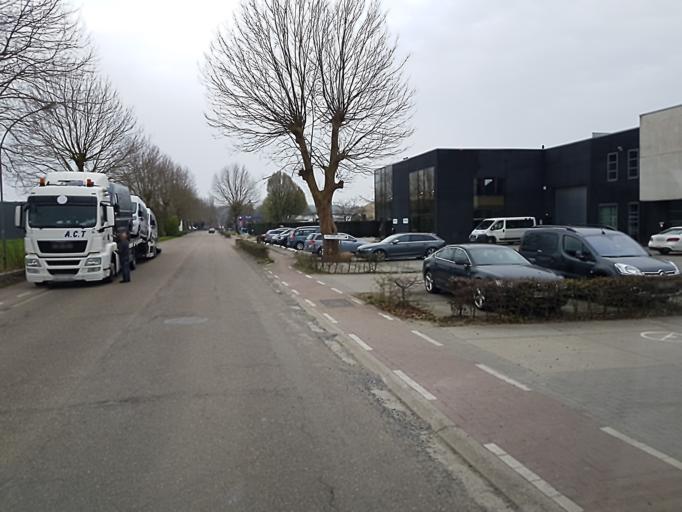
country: BE
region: Flanders
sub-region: Provincie Vlaams-Brabant
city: Aarschot
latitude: 50.9913
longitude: 4.8228
